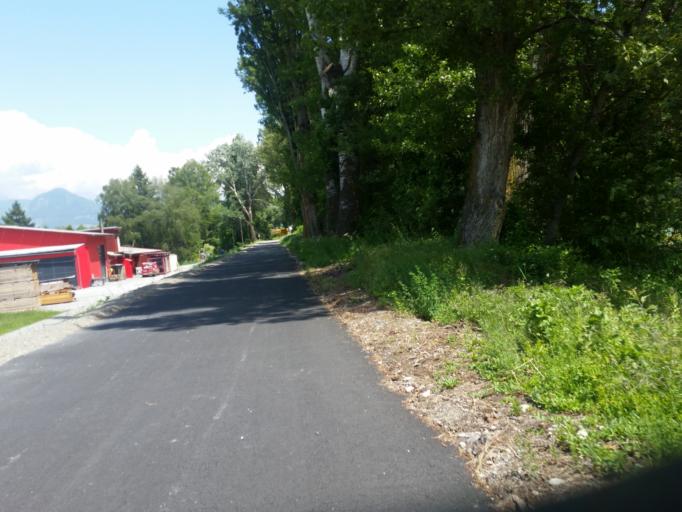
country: CH
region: Valais
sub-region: Sion District
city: Sitten
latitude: 46.2194
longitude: 7.3559
